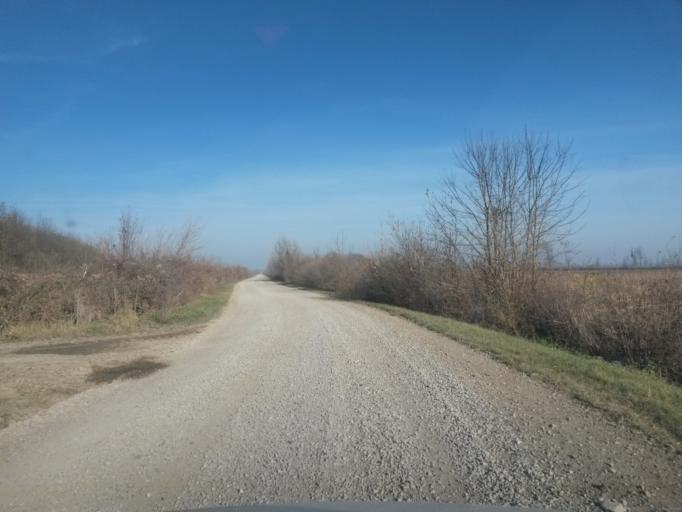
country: HR
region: Vukovarsko-Srijemska
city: Mirkovci
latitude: 45.2269
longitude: 18.8796
